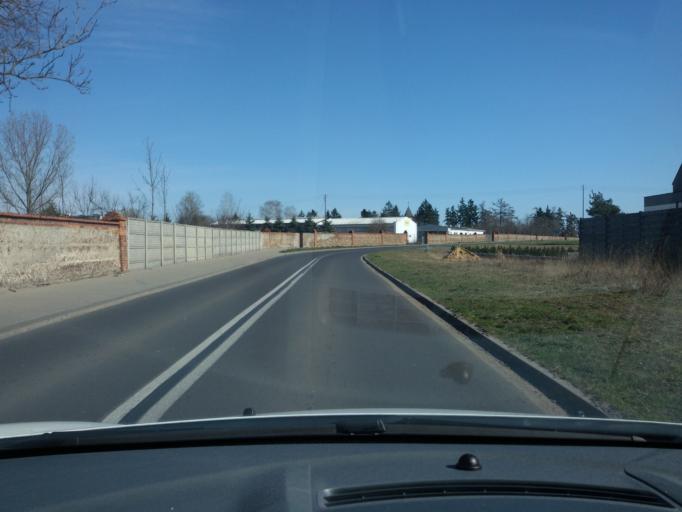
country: PL
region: Greater Poland Voivodeship
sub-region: Powiat leszczynski
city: Rydzyna
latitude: 51.7801
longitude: 16.6733
